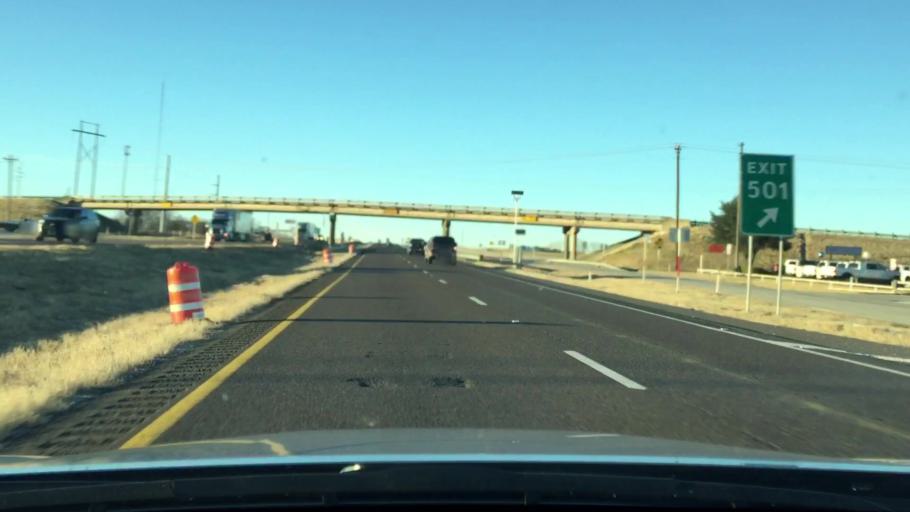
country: US
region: Texas
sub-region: Cooke County
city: Gainesville
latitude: 33.6803
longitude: -97.1554
